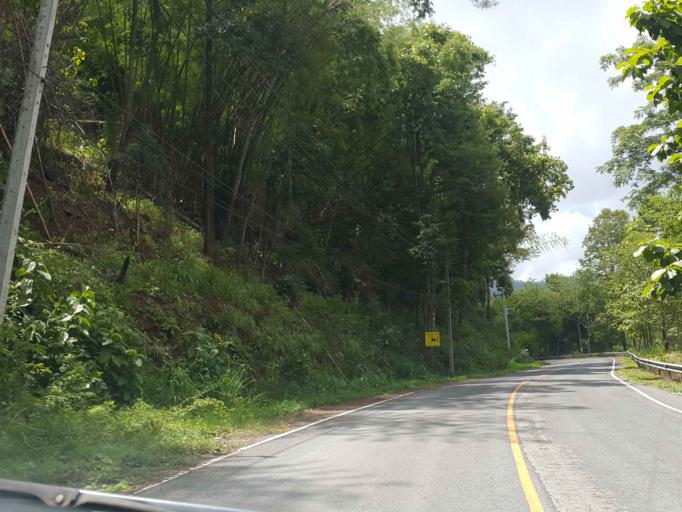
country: TH
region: Chiang Mai
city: Samoeng
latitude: 18.8140
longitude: 98.7892
